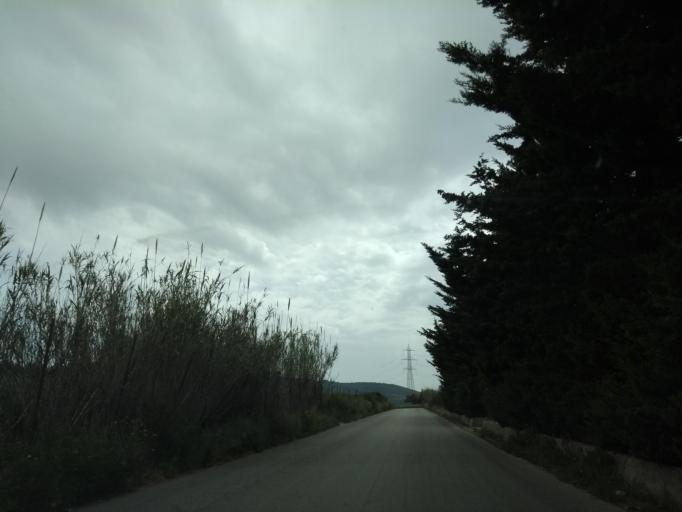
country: IT
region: Sicily
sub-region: Palermo
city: Partinico
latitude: 37.9952
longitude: 13.0657
